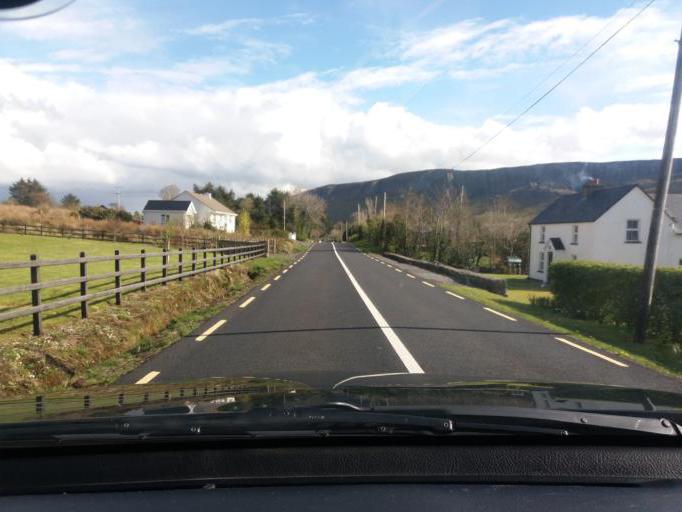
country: IE
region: Connaught
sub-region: County Leitrim
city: Kinlough
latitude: 54.3840
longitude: -8.2984
